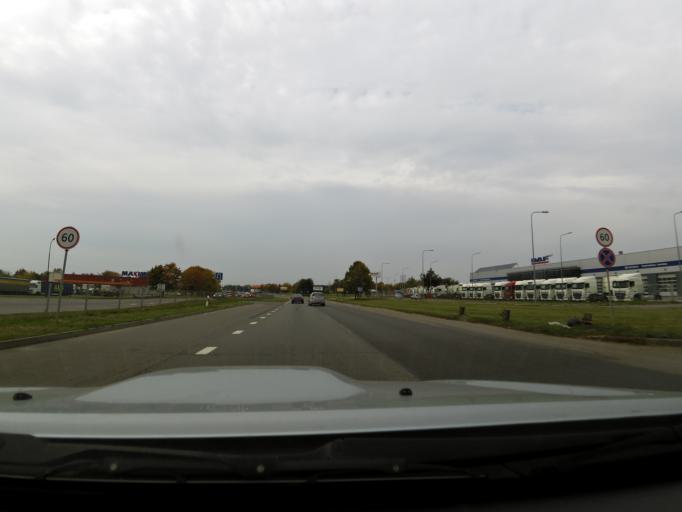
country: LT
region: Vilnius County
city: Rasos
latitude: 54.6525
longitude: 25.3083
